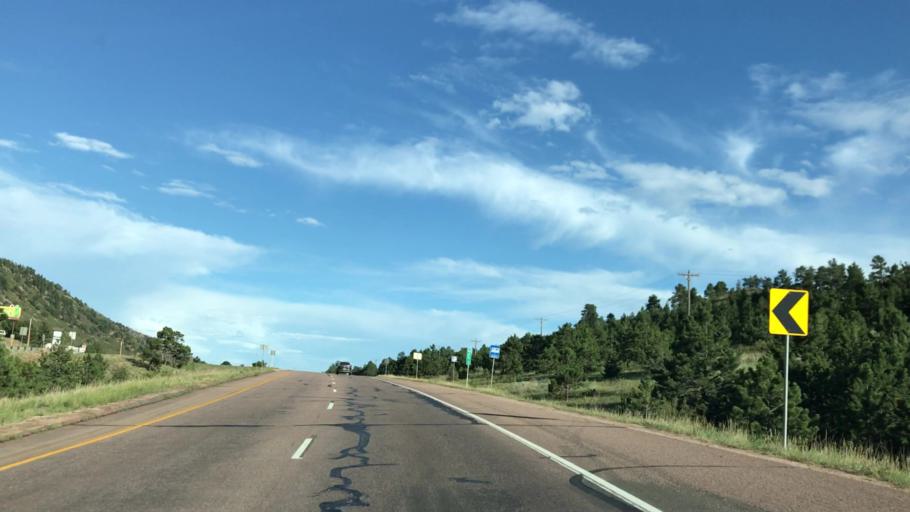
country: US
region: Colorado
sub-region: El Paso County
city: Cascade-Chipita Park
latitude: 38.9365
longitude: -105.0098
